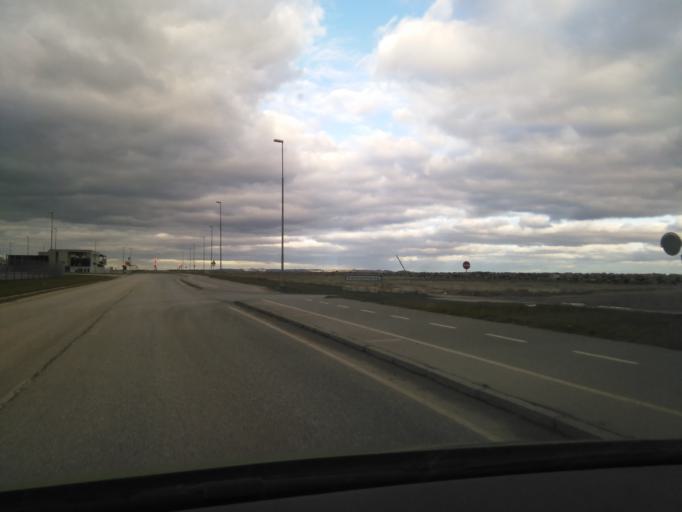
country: DK
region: Central Jutland
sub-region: Arhus Kommune
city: Arhus
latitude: 56.1452
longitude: 10.2384
